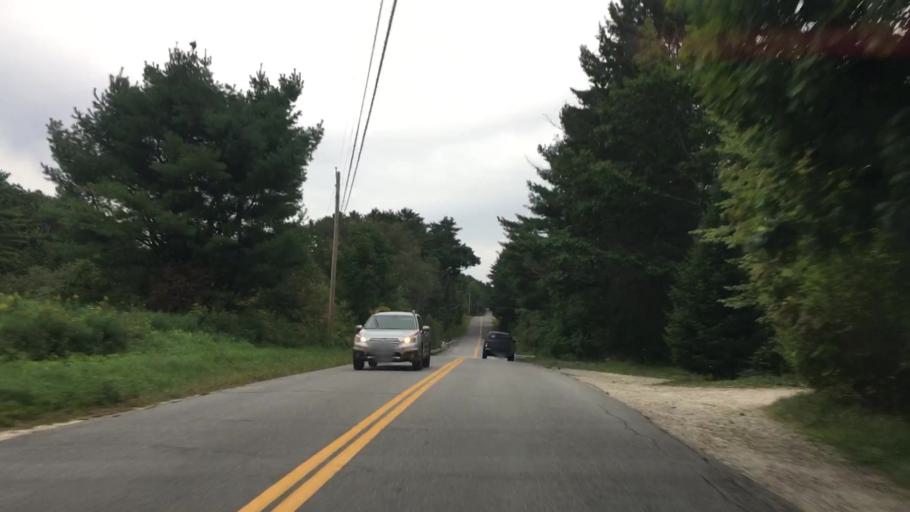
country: US
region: Maine
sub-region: Cumberland County
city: Freeport
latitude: 43.8839
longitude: -70.1672
